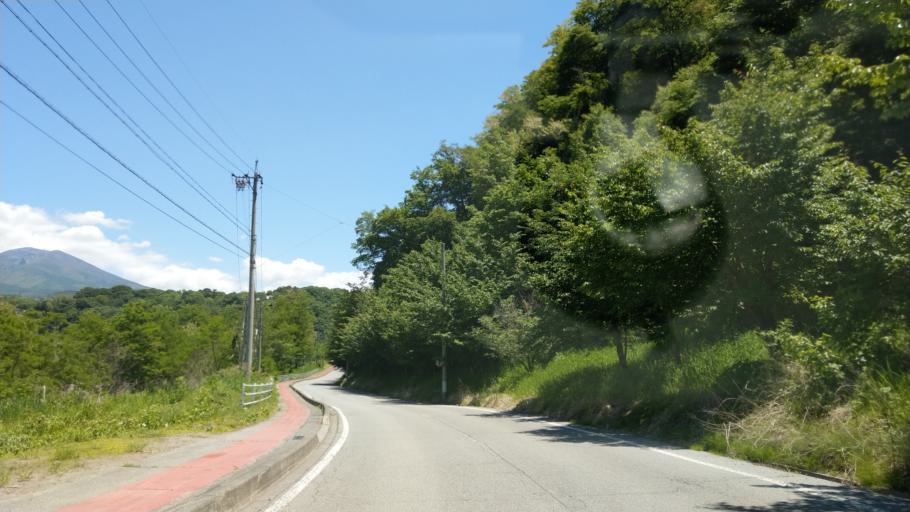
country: JP
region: Nagano
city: Komoro
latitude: 36.3250
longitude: 138.4069
